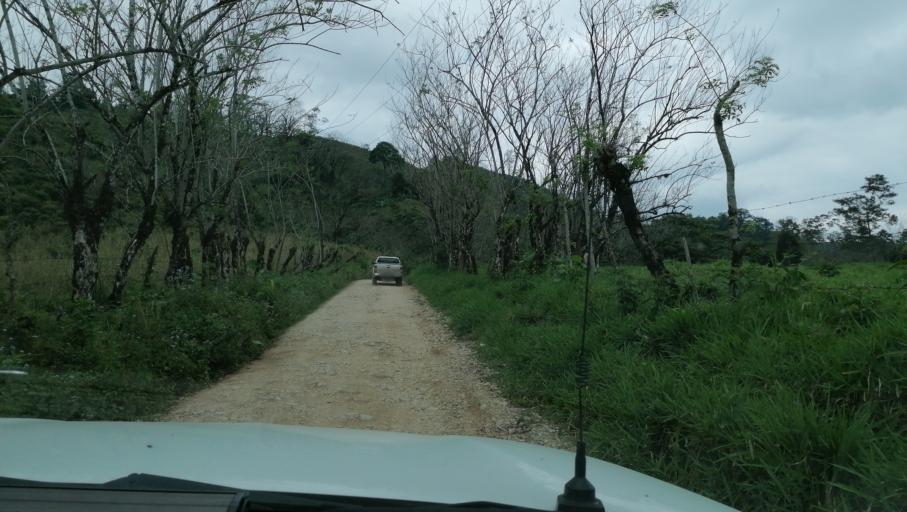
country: MX
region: Chiapas
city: Ocotepec
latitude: 17.2731
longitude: -93.2253
